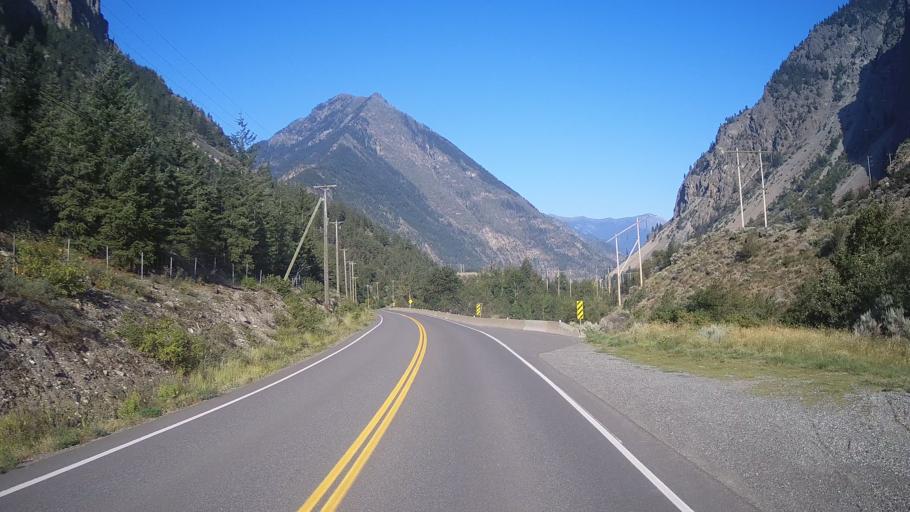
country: CA
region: British Columbia
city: Lillooet
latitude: 50.6691
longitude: -121.9577
